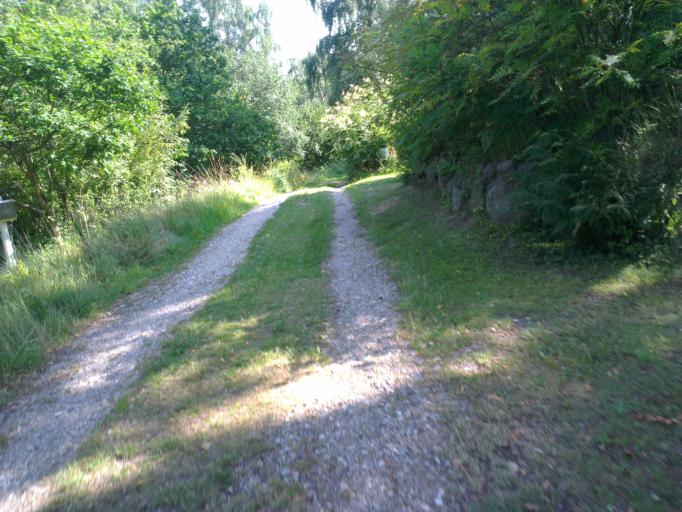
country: DK
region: Capital Region
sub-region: Halsnaes Kommune
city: Hundested
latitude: 55.9264
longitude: 11.9271
